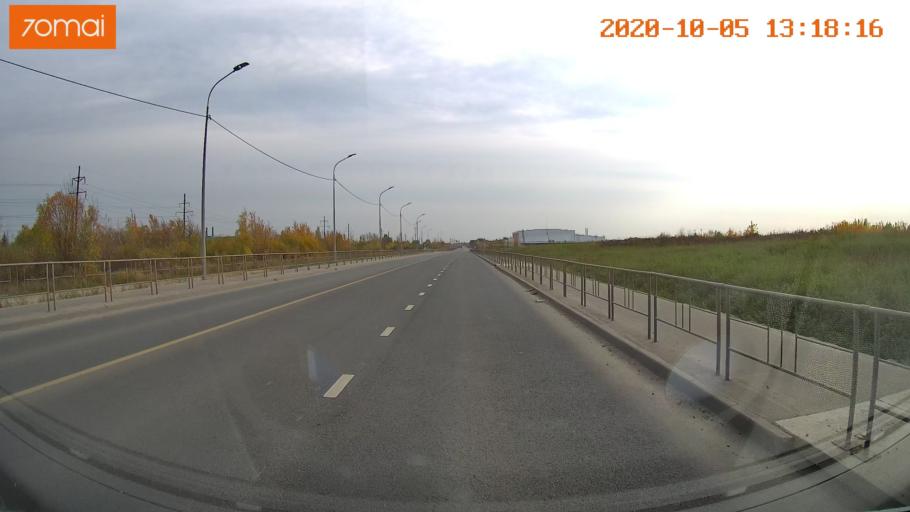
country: RU
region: Ivanovo
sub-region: Gorod Ivanovo
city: Ivanovo
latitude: 56.9788
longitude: 40.9184
